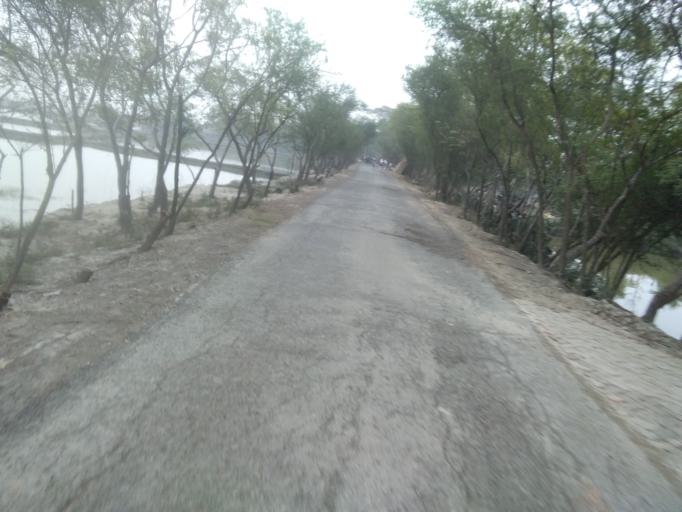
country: BD
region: Khulna
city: Satkhira
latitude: 22.5791
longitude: 89.0700
